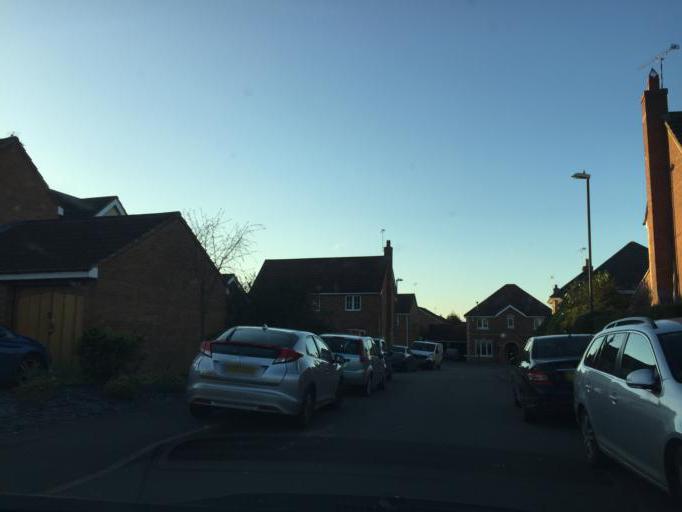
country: GB
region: England
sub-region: Warwickshire
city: Ryton on Dunsmore
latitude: 52.3997
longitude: -1.4346
